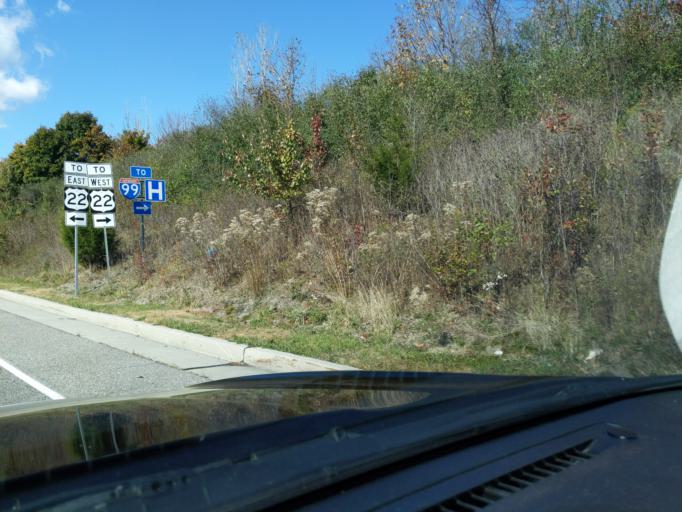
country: US
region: Pennsylvania
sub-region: Blair County
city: Lakemont
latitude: 40.4523
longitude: -78.4078
